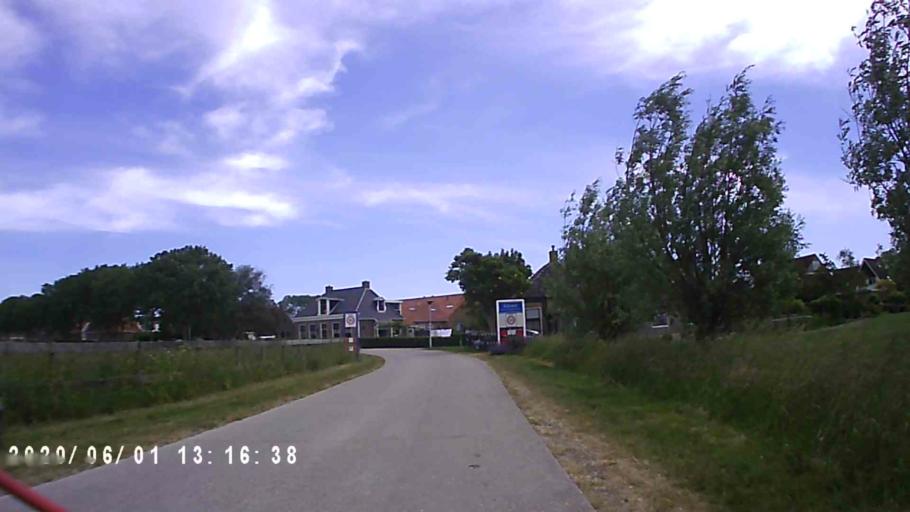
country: NL
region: Friesland
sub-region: Gemeente Littenseradiel
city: Wommels
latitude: 53.1191
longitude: 5.5675
